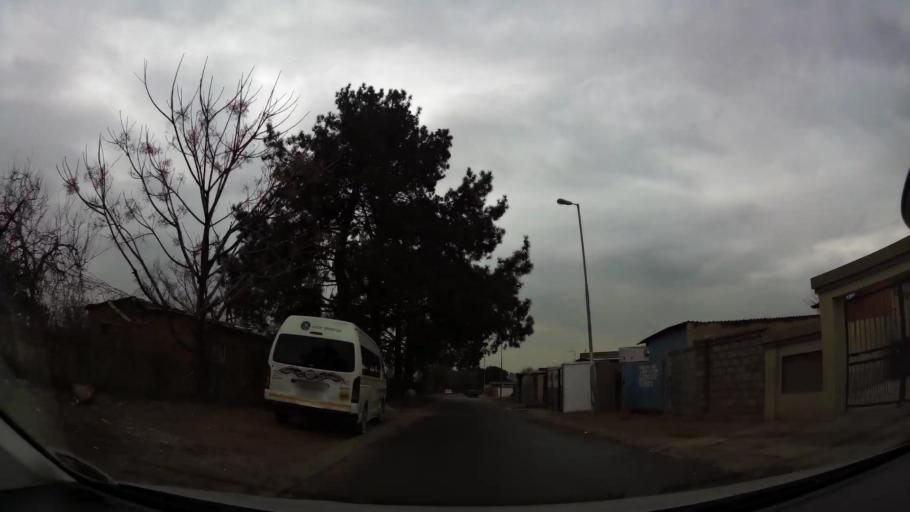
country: ZA
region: Gauteng
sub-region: City of Johannesburg Metropolitan Municipality
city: Soweto
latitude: -26.2522
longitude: 27.8733
